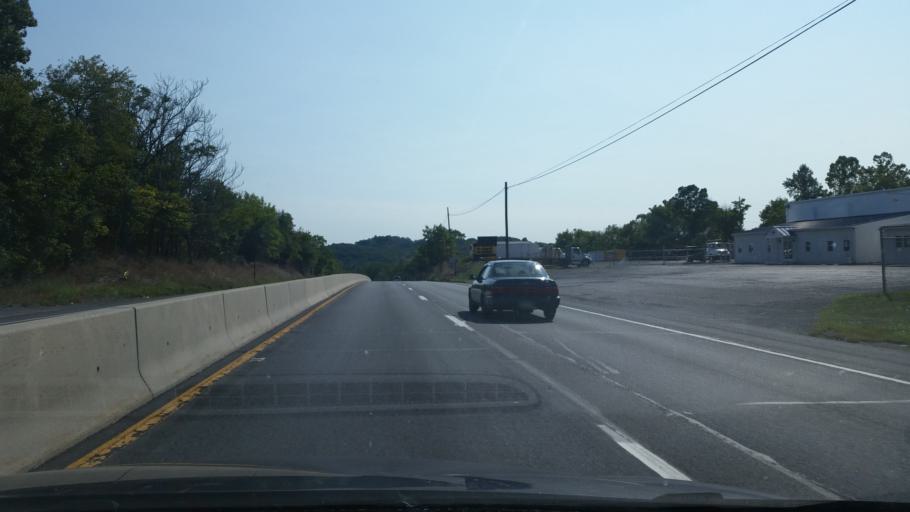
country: US
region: Pennsylvania
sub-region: Berks County
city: Leesport
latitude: 40.4696
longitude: -75.9692
